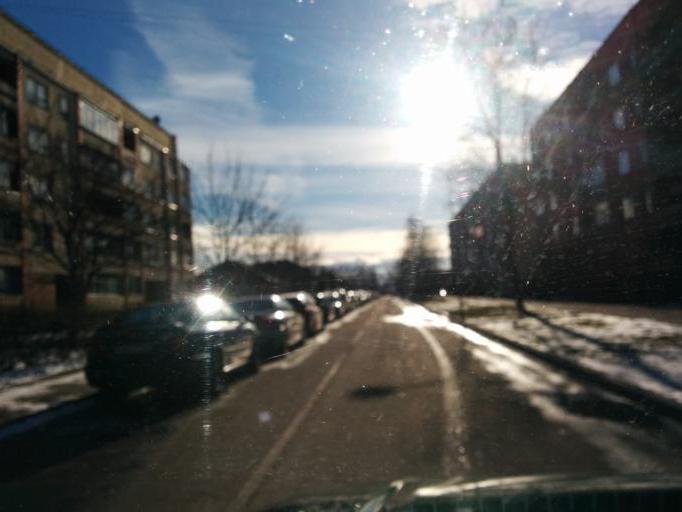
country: LV
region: Jelgava
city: Jelgava
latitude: 56.6561
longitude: 23.7071
